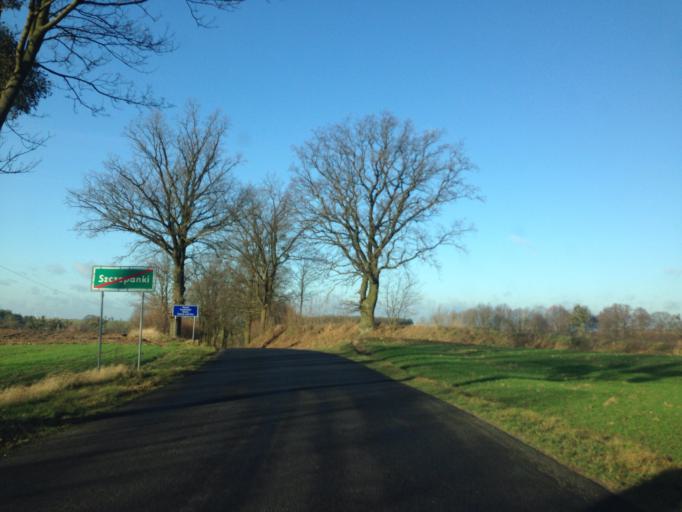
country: PL
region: Kujawsko-Pomorskie
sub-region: Powiat brodnicki
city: Jablonowo Pomorskie
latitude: 53.4136
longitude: 19.1336
